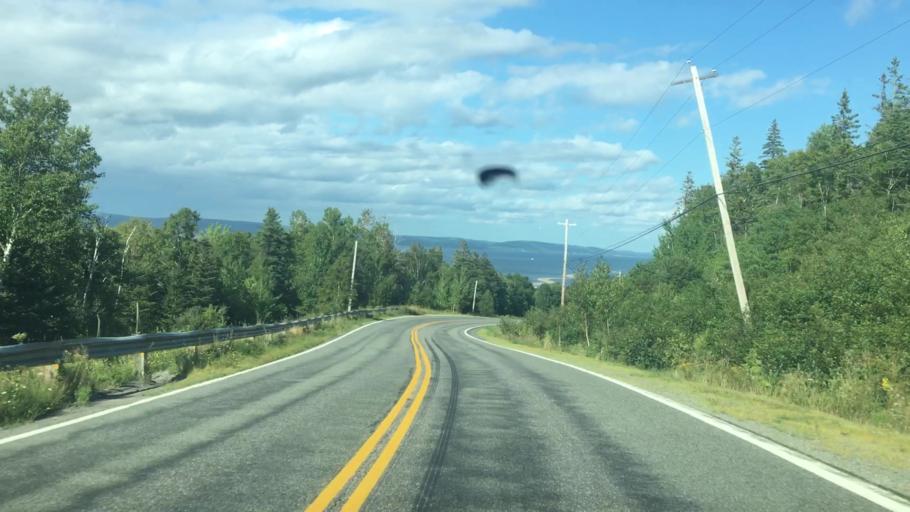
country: CA
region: Nova Scotia
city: Sydney
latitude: 45.8651
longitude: -60.6225
